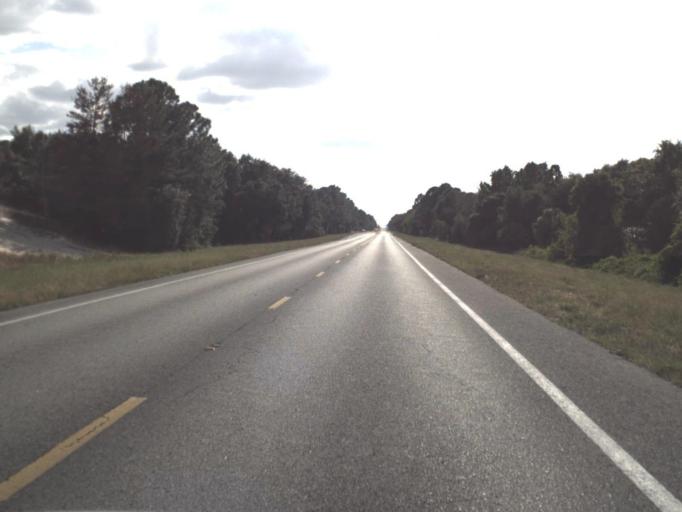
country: US
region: Florida
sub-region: Brevard County
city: Port Saint John
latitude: 28.5220
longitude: -80.8248
